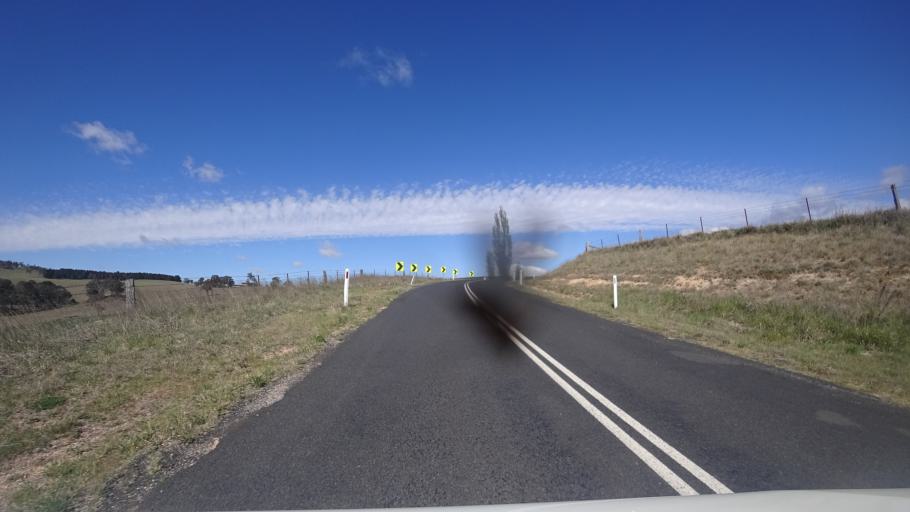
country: AU
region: New South Wales
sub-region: Lithgow
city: Portland
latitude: -33.5189
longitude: 149.9516
